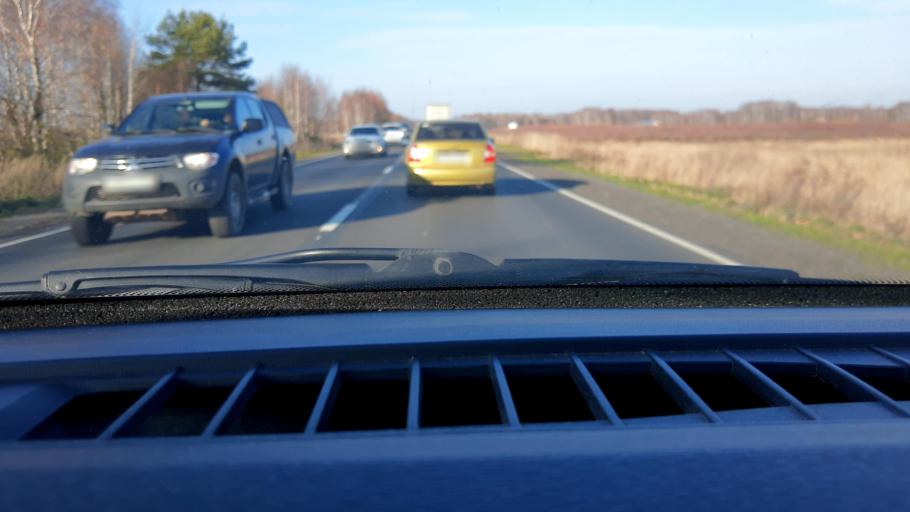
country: RU
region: Nizjnij Novgorod
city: Novaya Balakhna
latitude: 56.5783
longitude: 43.6938
